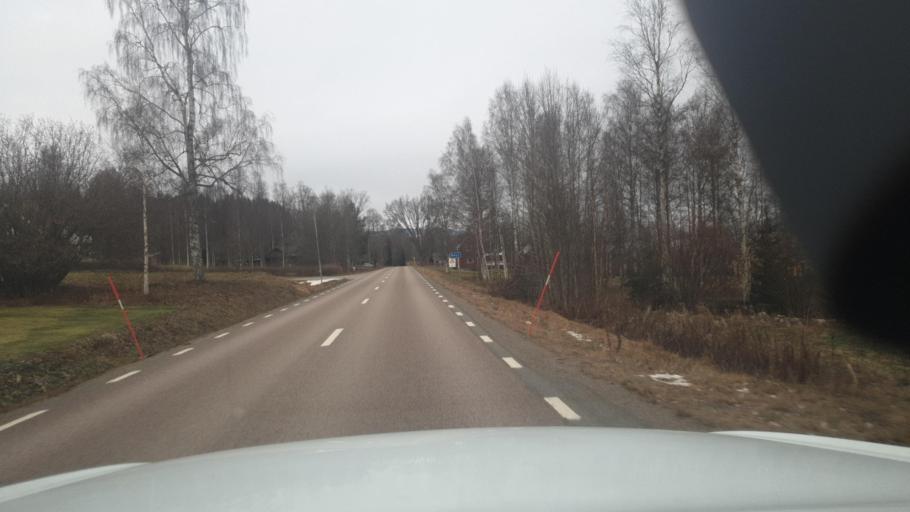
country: SE
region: Vaermland
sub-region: Sunne Kommun
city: Sunne
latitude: 59.8865
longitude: 12.9234
